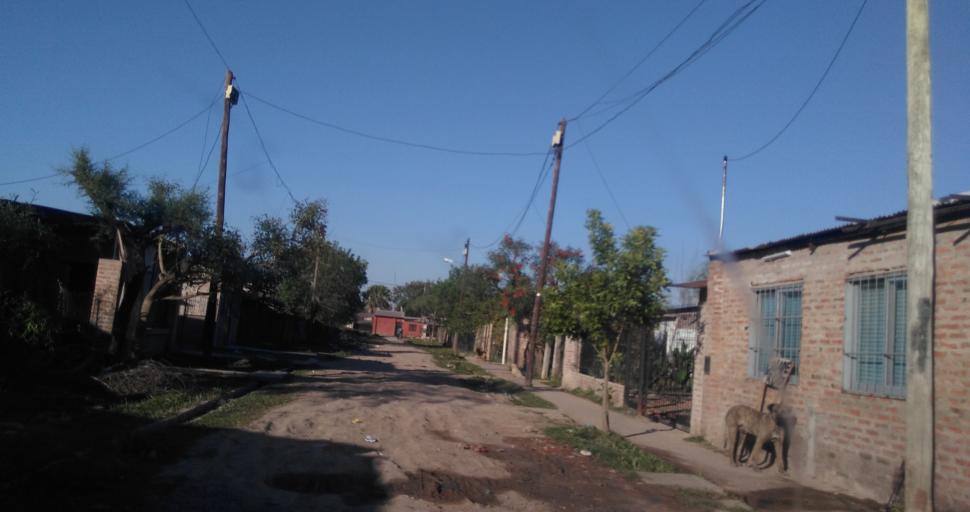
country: AR
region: Chaco
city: Resistencia
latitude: -27.4763
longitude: -59.0087
